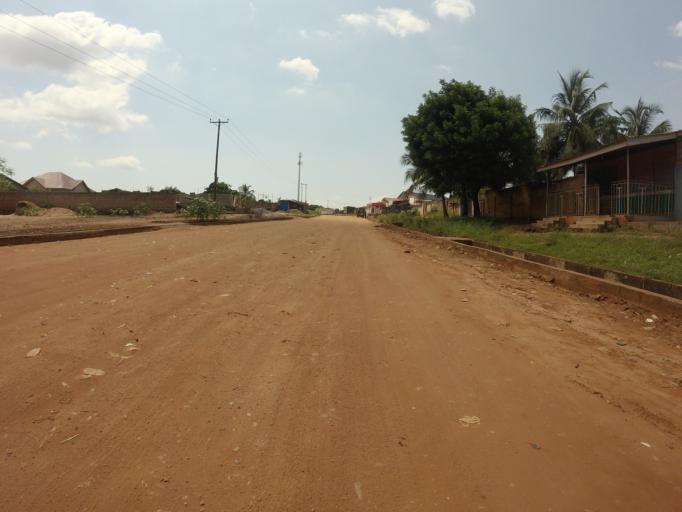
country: GH
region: Greater Accra
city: Gbawe
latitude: 5.6197
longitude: -0.3075
